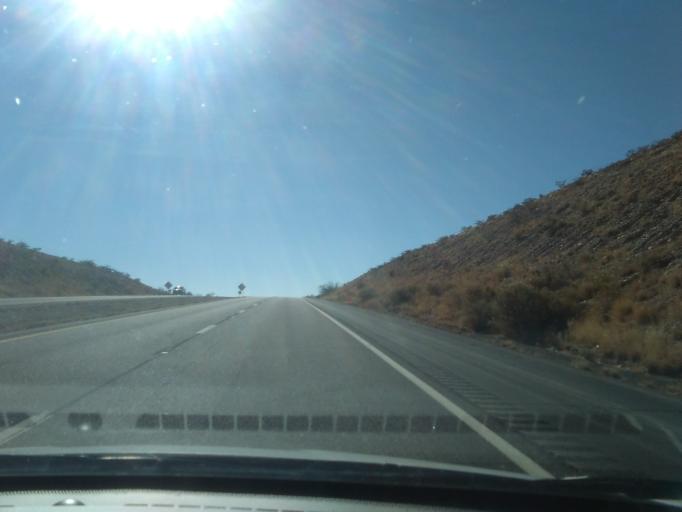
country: US
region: New Mexico
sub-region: Sierra County
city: Elephant Butte
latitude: 33.5293
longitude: -107.1937
